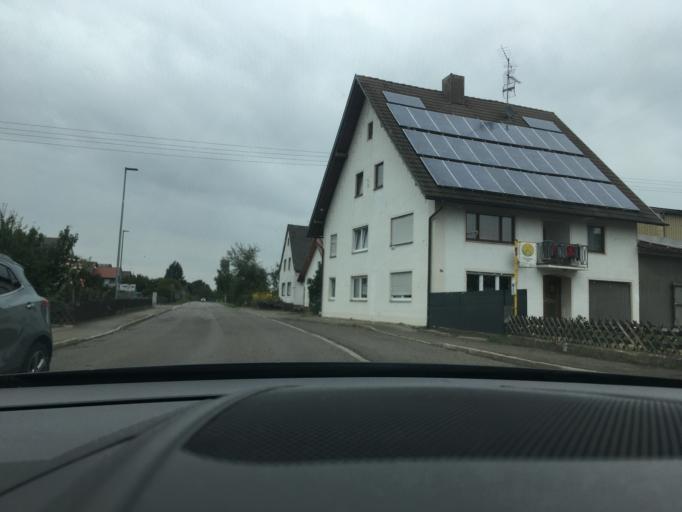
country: DE
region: Baden-Wuerttemberg
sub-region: Tuebingen Region
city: Kirchdorf
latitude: 48.0470
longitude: 10.1229
